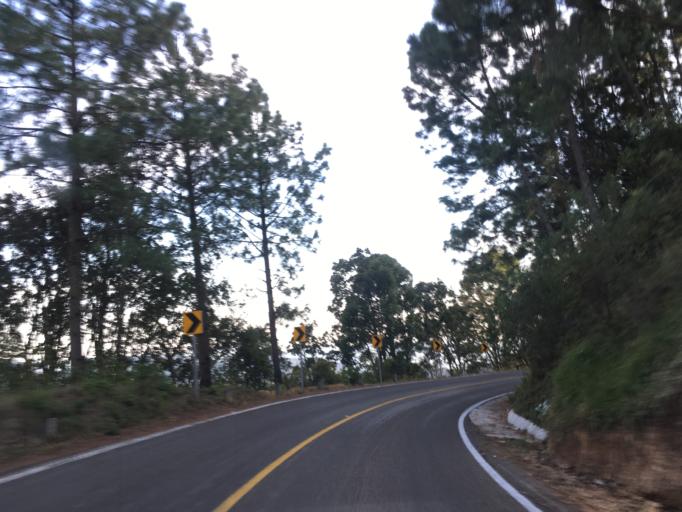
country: MX
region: Michoacan
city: Tzitzio
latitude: 19.6686
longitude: -100.9054
